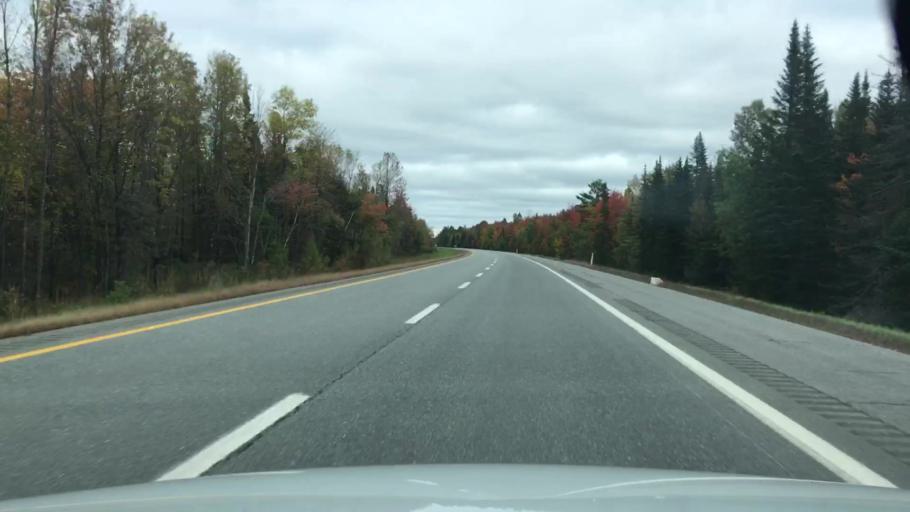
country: US
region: Maine
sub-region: Kennebec County
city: Clinton
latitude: 44.6665
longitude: -69.4909
